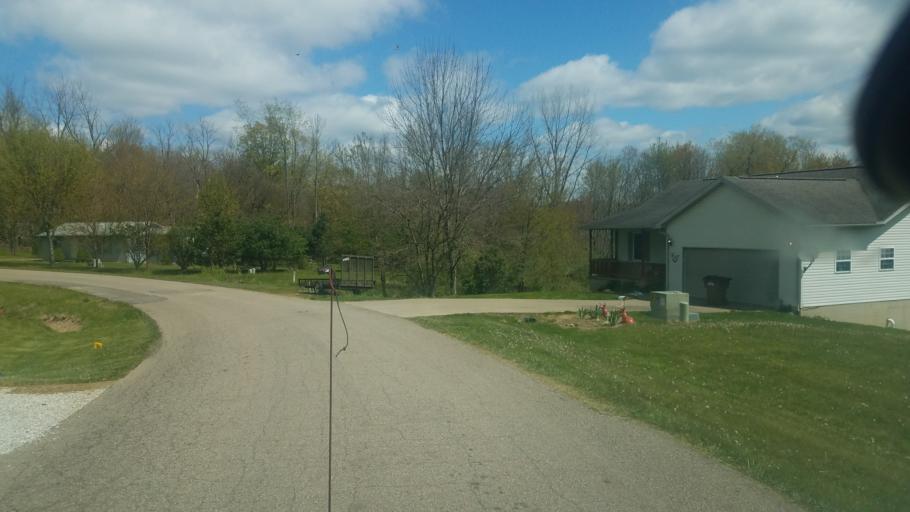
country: US
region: Ohio
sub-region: Knox County
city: Danville
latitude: 40.4597
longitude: -82.3403
